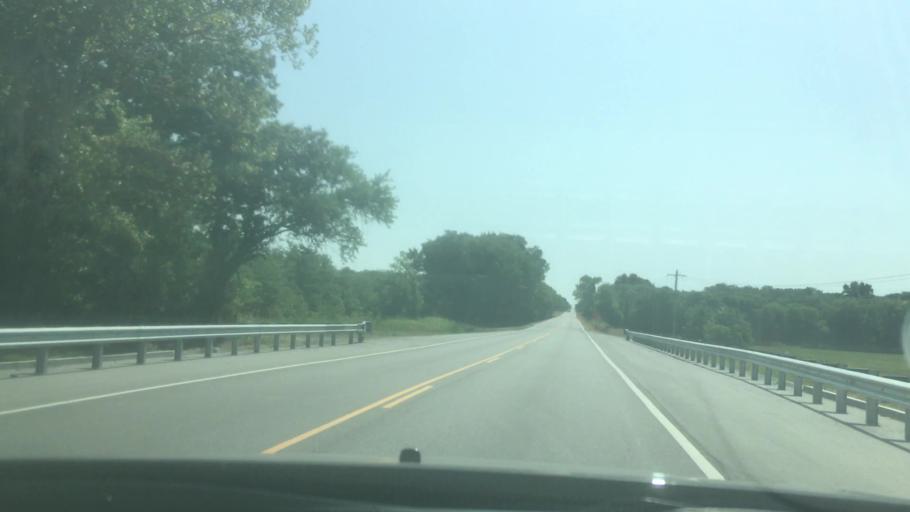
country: US
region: Oklahoma
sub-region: Bryan County
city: Durant
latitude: 34.1427
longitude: -96.4002
